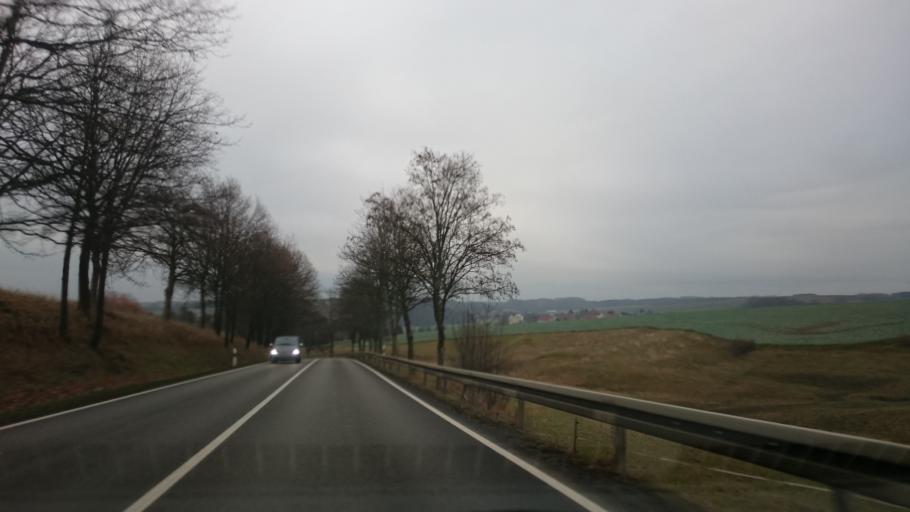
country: DE
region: Saxony
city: Mulsen
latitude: 50.7337
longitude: 12.5658
